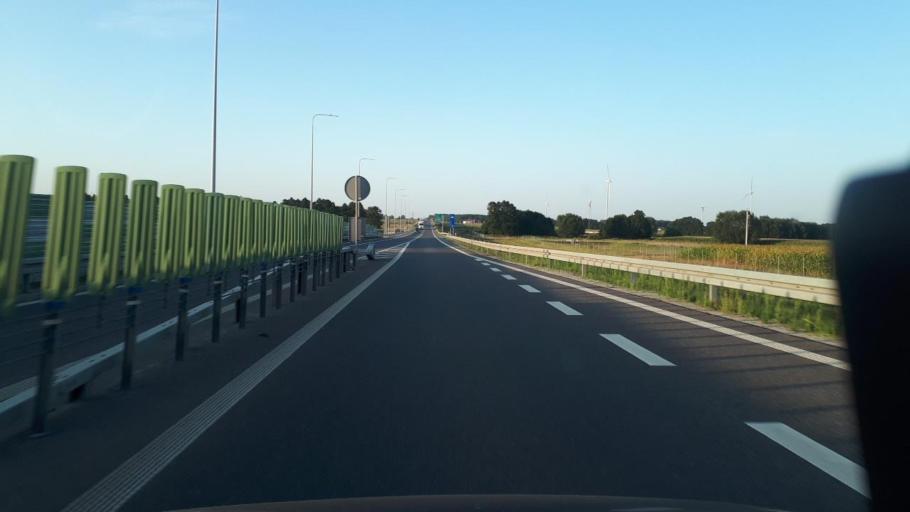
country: PL
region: Greater Poland Voivodeship
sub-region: Powiat kepinski
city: Baranow
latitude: 51.2597
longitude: 18.0173
